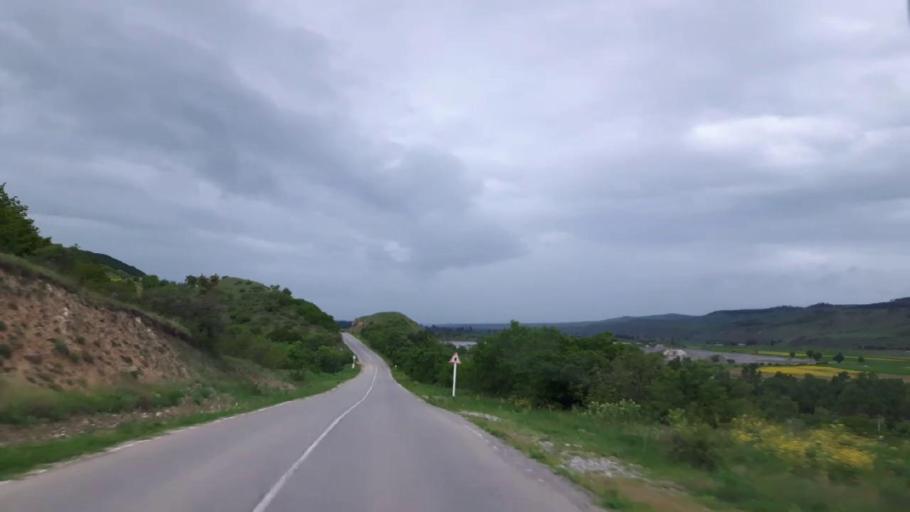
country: GE
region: Shida Kartli
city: Gori
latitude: 41.9885
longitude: 44.0425
